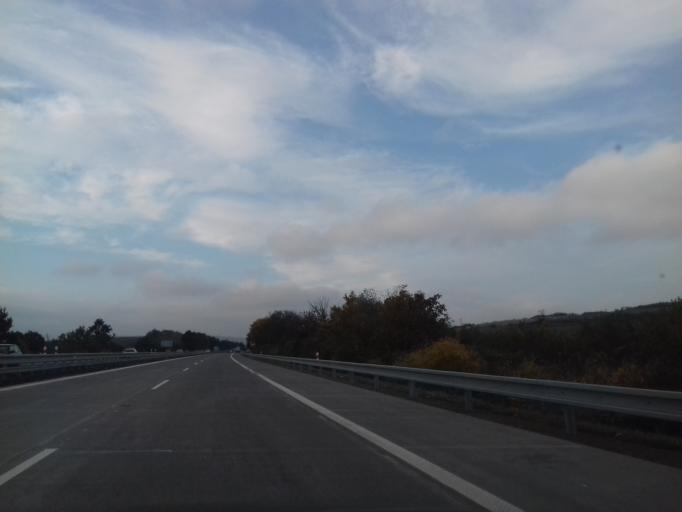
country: CZ
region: South Moravian
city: Velke Nemcice
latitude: 48.9789
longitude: 16.6982
